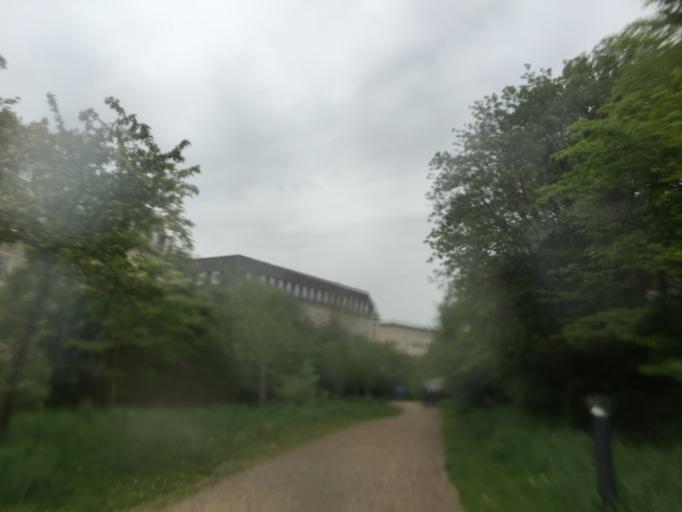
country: DK
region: Capital Region
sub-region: Kobenhavn
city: Vanlose
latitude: 55.6857
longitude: 12.5056
